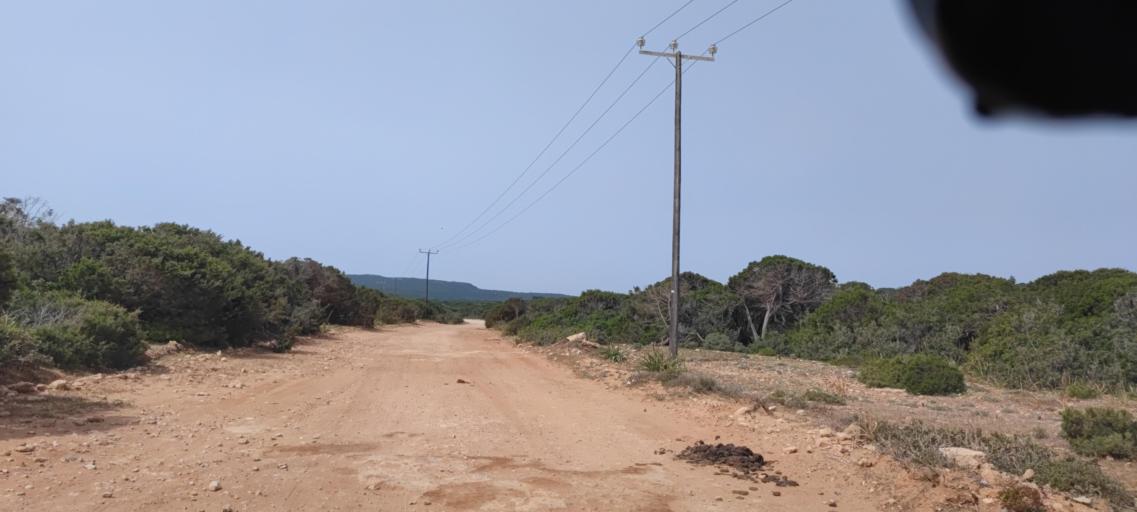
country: CY
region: Ammochostos
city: Rizokarpaso
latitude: 35.6715
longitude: 34.5743
